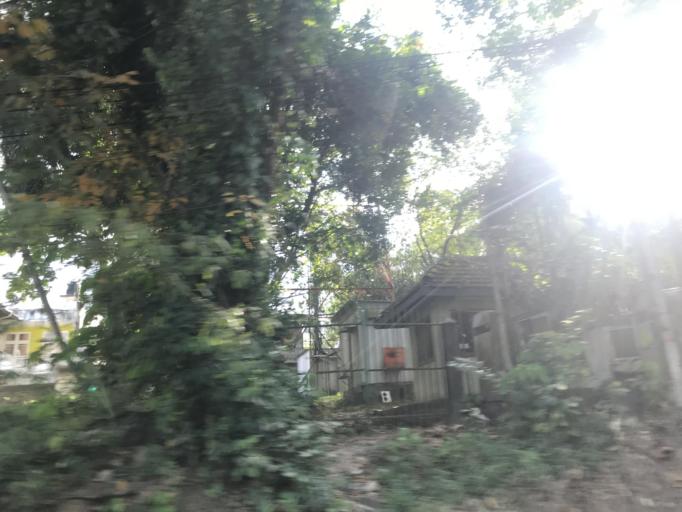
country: LK
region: Western
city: Gampaha
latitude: 7.0641
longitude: 80.0099
